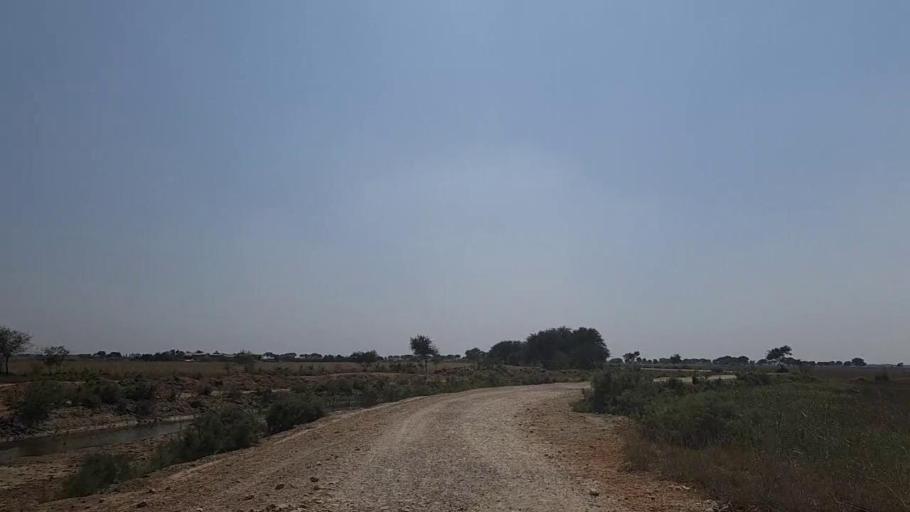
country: PK
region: Sindh
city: Jati
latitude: 24.5412
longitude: 68.3162
